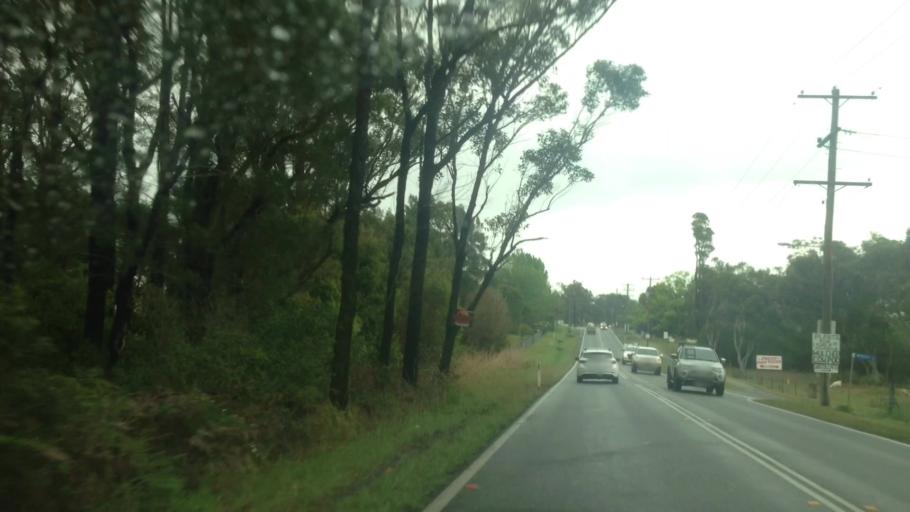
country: AU
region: New South Wales
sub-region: Wyong Shire
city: Charmhaven
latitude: -33.1722
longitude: 151.4783
